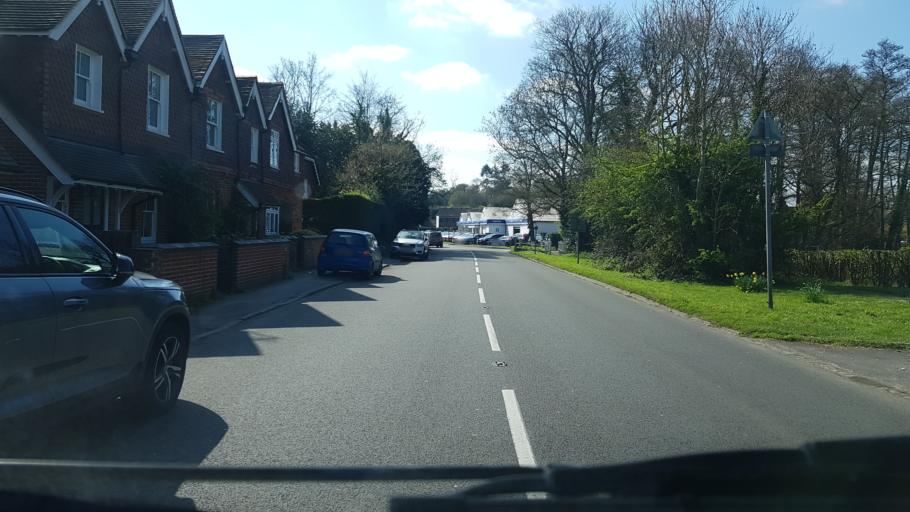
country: GB
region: England
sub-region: Surrey
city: Pirbright
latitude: 51.2927
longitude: -0.6458
